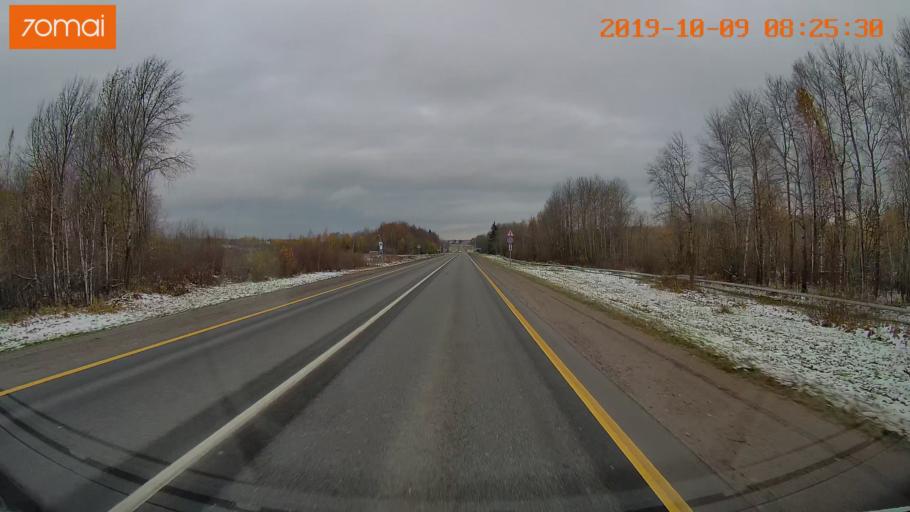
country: RU
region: Vologda
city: Gryazovets
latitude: 58.7821
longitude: 40.2719
